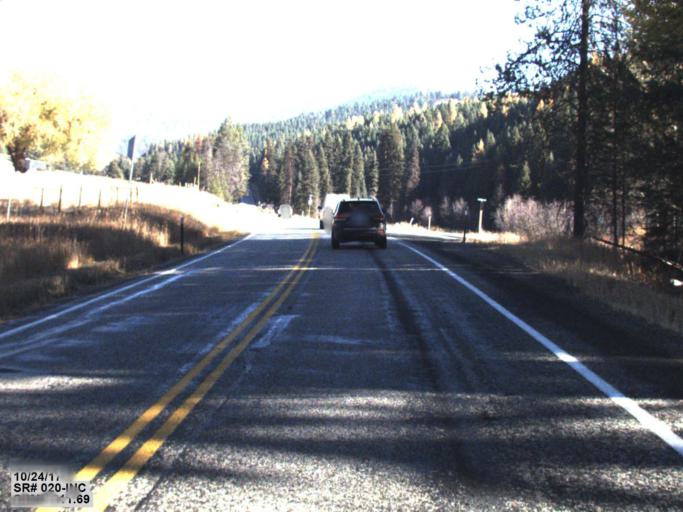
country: US
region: Washington
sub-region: Ferry County
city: Republic
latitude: 48.6043
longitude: -118.6026
